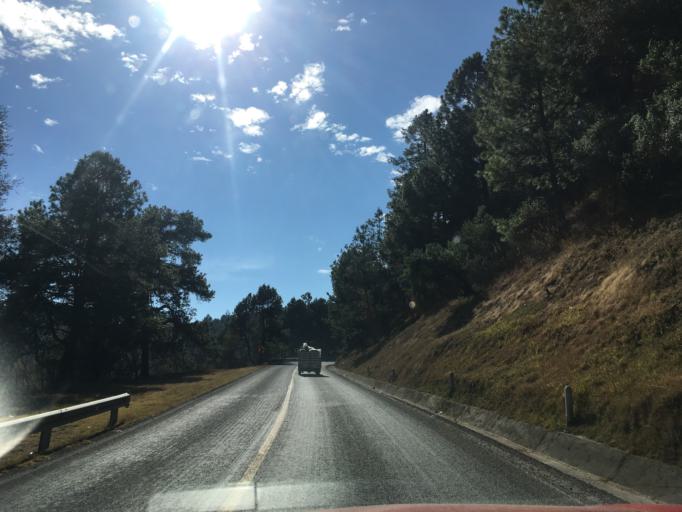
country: MX
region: Michoacan
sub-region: Hidalgo
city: Tierras Coloradas (San Pedro)
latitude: 19.7113
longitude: -100.7495
